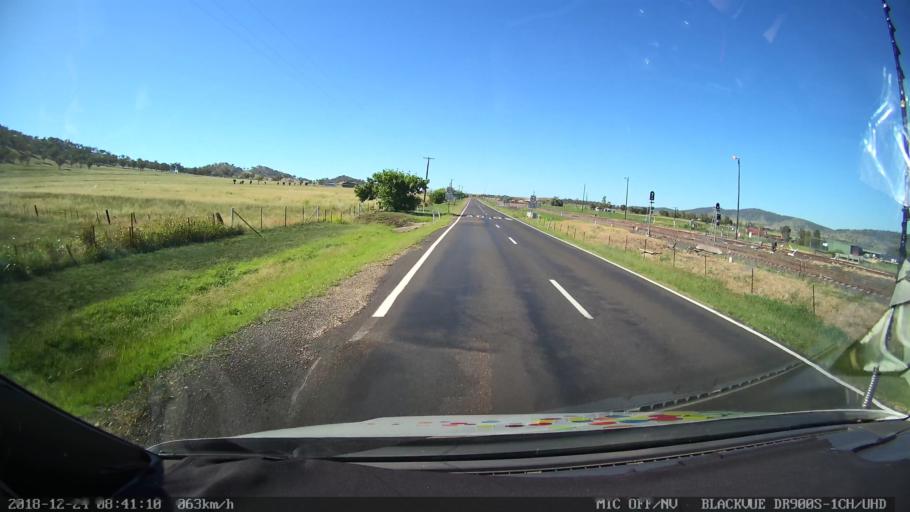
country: AU
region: New South Wales
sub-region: Liverpool Plains
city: Quirindi
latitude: -31.3604
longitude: 150.6454
